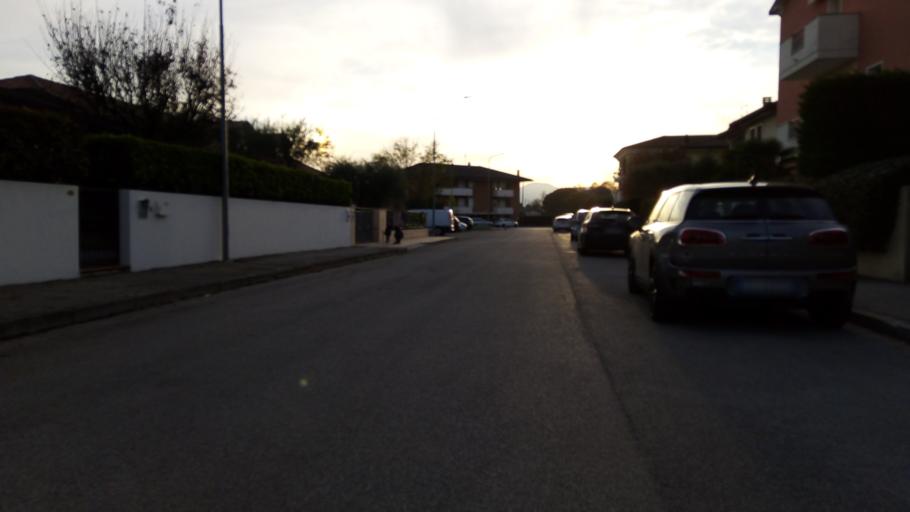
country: IT
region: Veneto
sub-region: Provincia di Padova
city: Abano Terme
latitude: 45.3674
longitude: 11.7897
